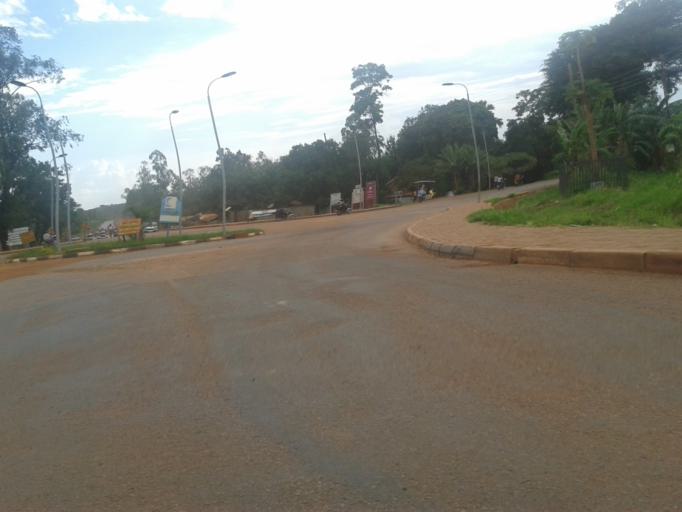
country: UG
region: Northern Region
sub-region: Gulu District
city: Gulu
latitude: 2.7614
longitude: 32.2796
